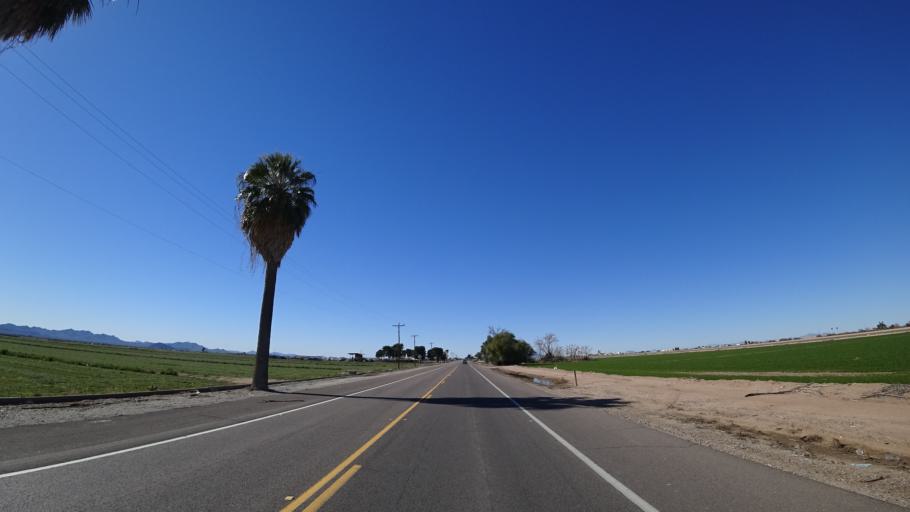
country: US
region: Arizona
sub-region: Maricopa County
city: Buckeye
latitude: 33.3703
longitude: -112.6088
